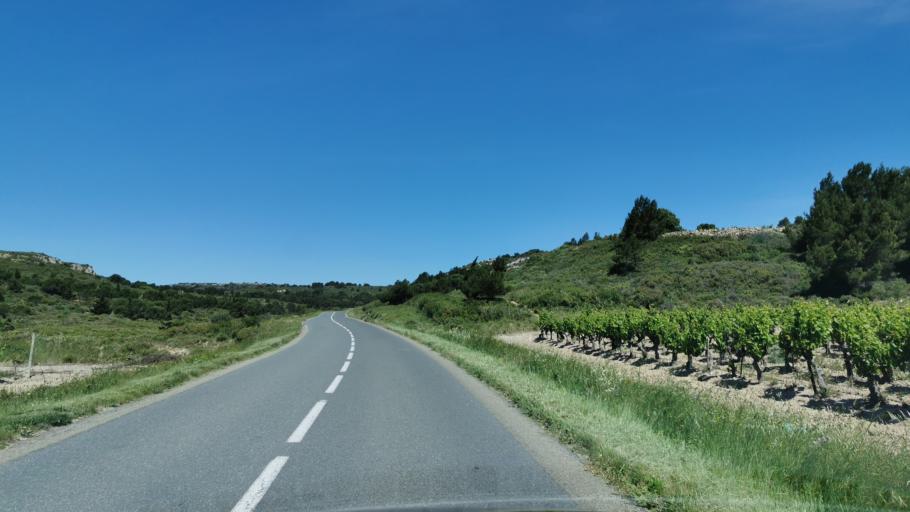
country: FR
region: Languedoc-Roussillon
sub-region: Departement de l'Aude
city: Armissan
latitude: 43.1596
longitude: 3.1492
